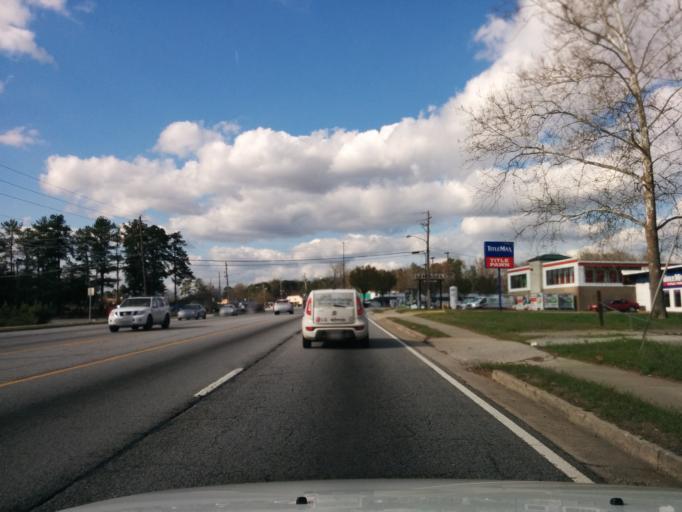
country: US
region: Georgia
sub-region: Fulton County
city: College Park
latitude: 33.6078
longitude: -84.4712
